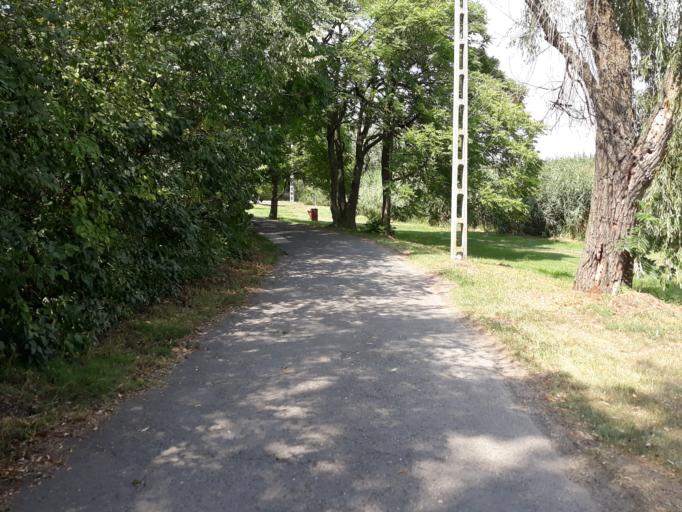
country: HU
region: Bekes
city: Oroshaza
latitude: 46.5628
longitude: 20.6247
